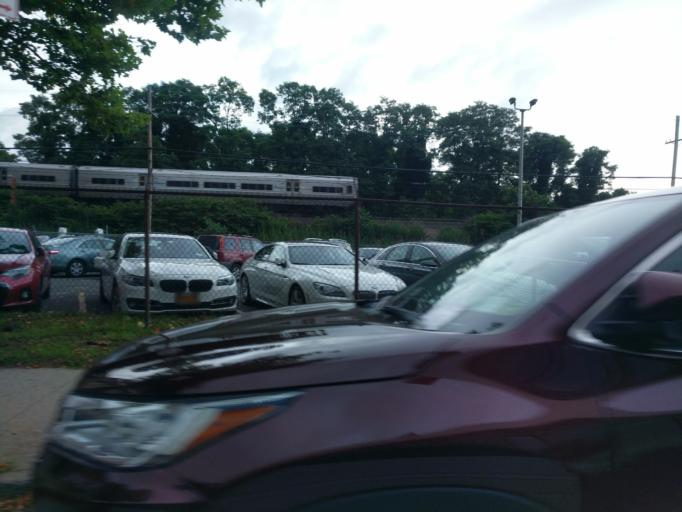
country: US
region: New York
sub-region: Queens County
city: Jamaica
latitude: 40.6763
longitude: -73.7679
